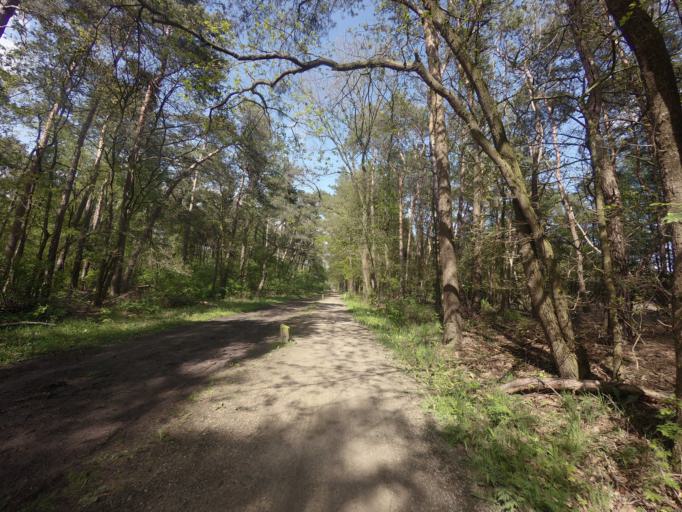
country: NL
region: Overijssel
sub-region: Gemeente Haaksbergen
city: Haaksbergen
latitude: 52.1639
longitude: 6.7883
